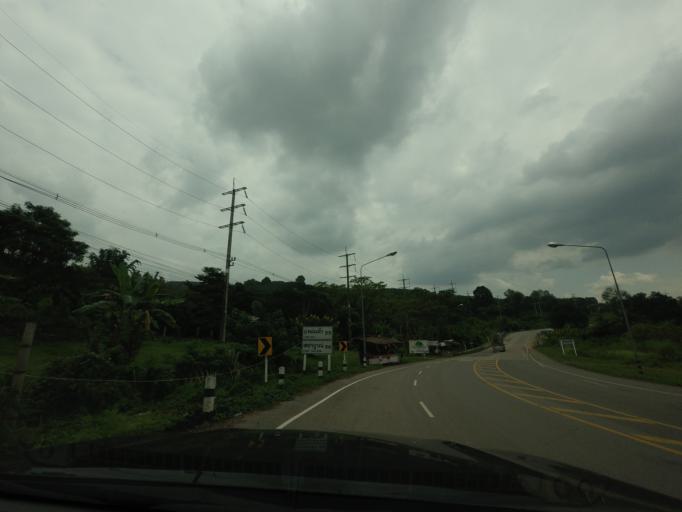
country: TH
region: Loei
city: Dan Sai
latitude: 17.2022
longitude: 101.1610
